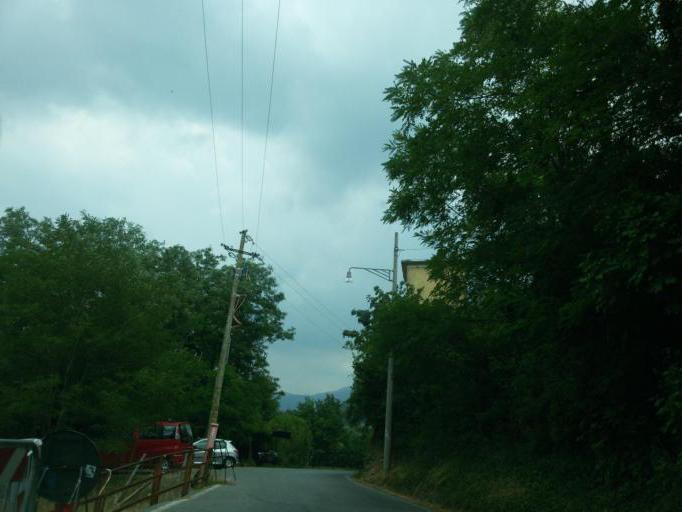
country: IT
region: Liguria
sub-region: Provincia di Genova
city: Piccarello
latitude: 44.4336
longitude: 9.0168
